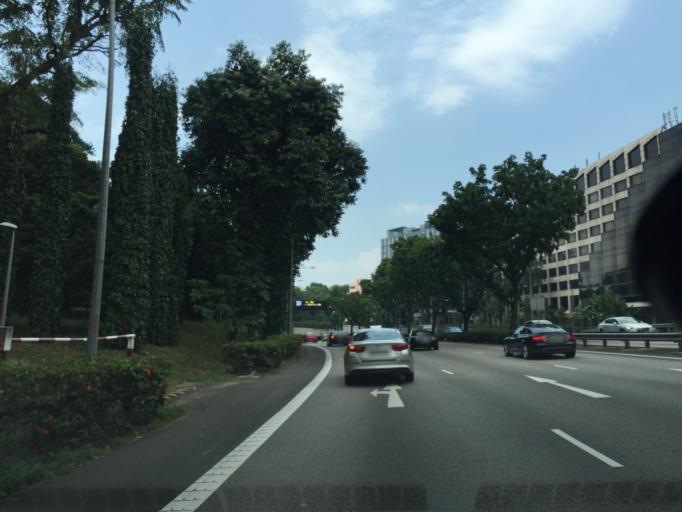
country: SG
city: Singapore
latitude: 1.3034
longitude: 103.8407
